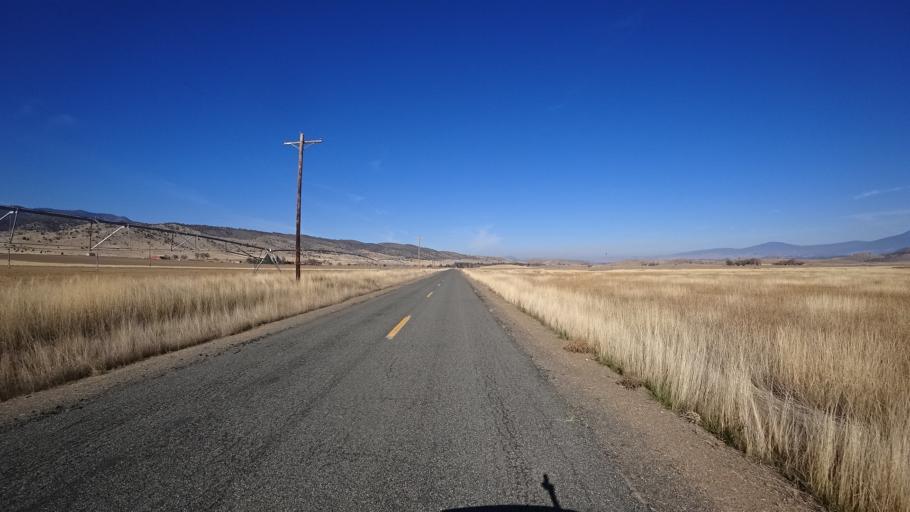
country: US
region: California
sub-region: Siskiyou County
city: Montague
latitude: 41.5664
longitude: -122.5490
